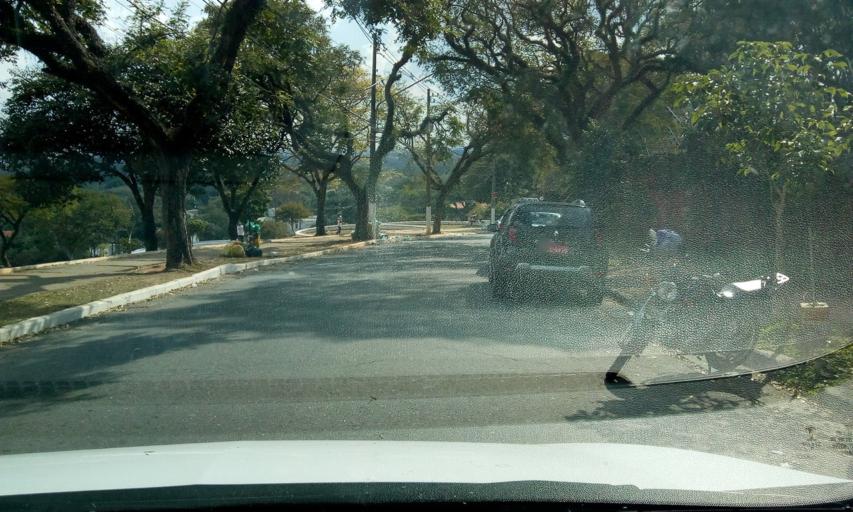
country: BR
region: Sao Paulo
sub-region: Sao Paulo
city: Sao Paulo
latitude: -23.5535
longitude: -46.7026
